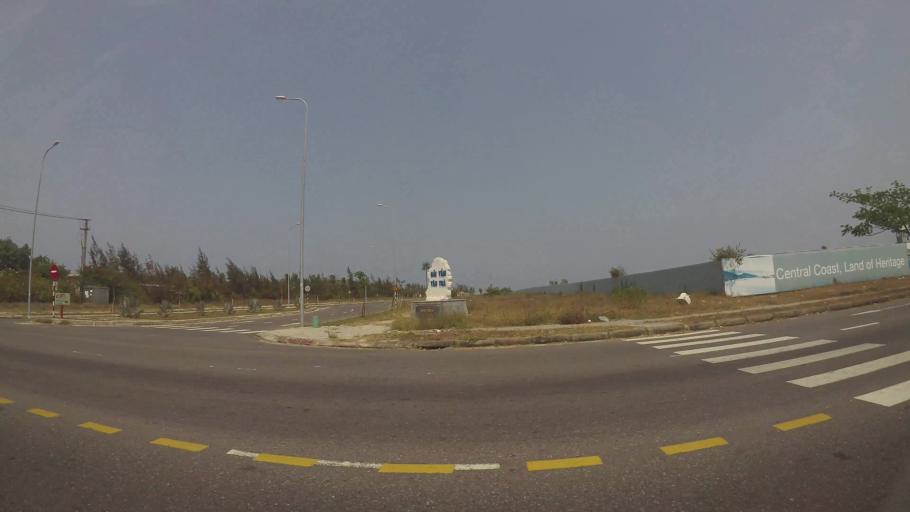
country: VN
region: Da Nang
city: Ngu Hanh Son
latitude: 15.9866
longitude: 108.2726
